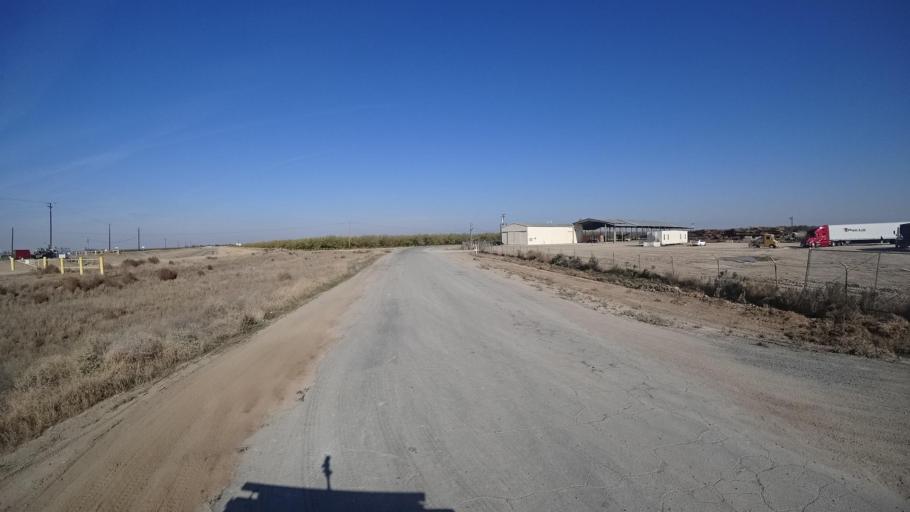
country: US
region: California
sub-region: Kern County
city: McFarland
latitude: 35.6445
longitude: -119.2040
